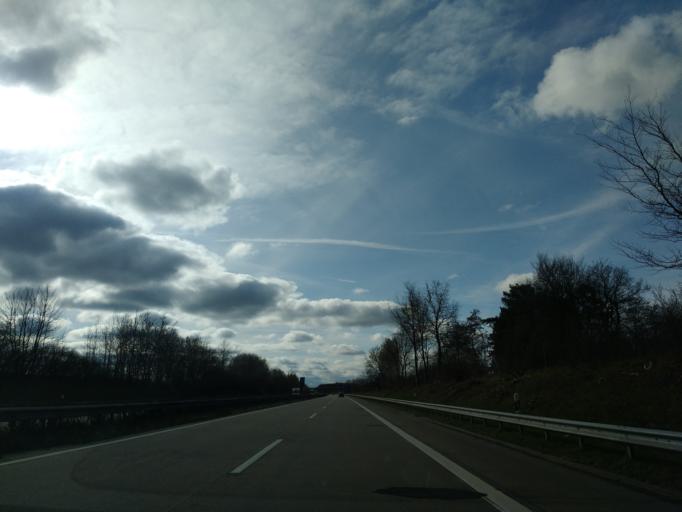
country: DE
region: Lower Saxony
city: Midlum
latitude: 53.6869
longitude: 8.6597
